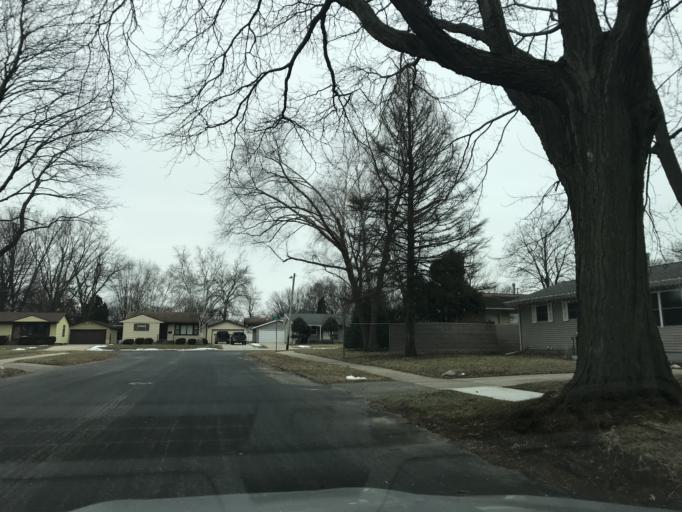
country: US
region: Wisconsin
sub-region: Dane County
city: Monona
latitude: 43.0943
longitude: -89.3034
